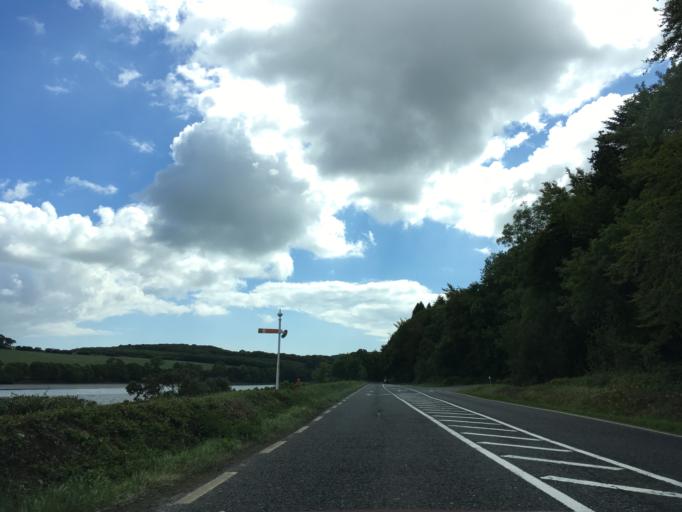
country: IE
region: Munster
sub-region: County Cork
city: Crosshaven
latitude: 51.8089
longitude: -8.3482
